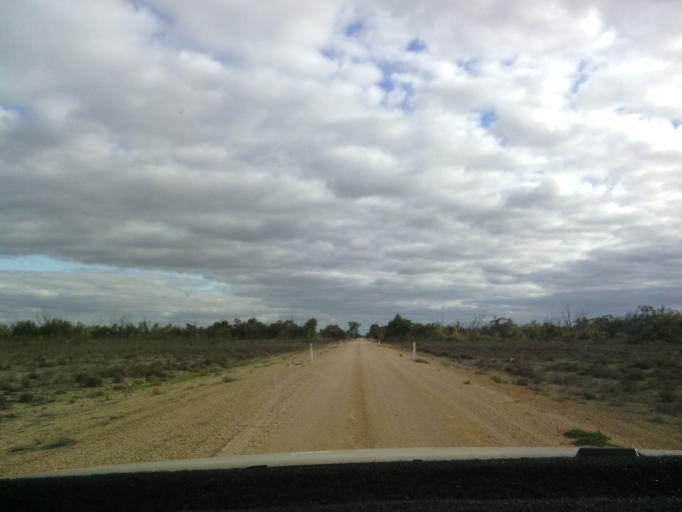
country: AU
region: South Australia
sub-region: Renmark Paringa
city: Renmark
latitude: -34.1646
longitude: 141.1939
